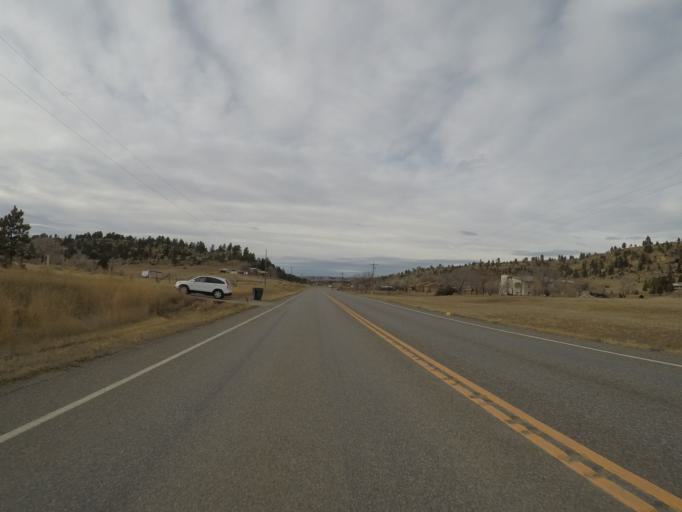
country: US
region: Montana
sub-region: Yellowstone County
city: Laurel
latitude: 45.8189
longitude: -108.6966
